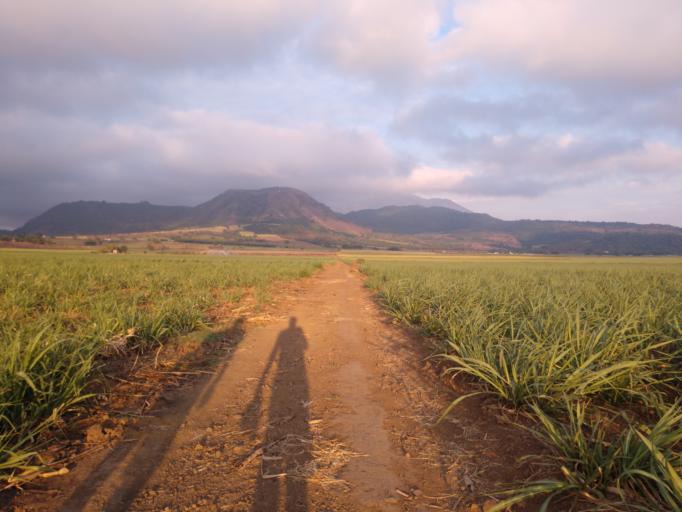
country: MX
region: Nayarit
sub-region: Tepic
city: La Corregidora
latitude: 21.4845
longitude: -104.8072
